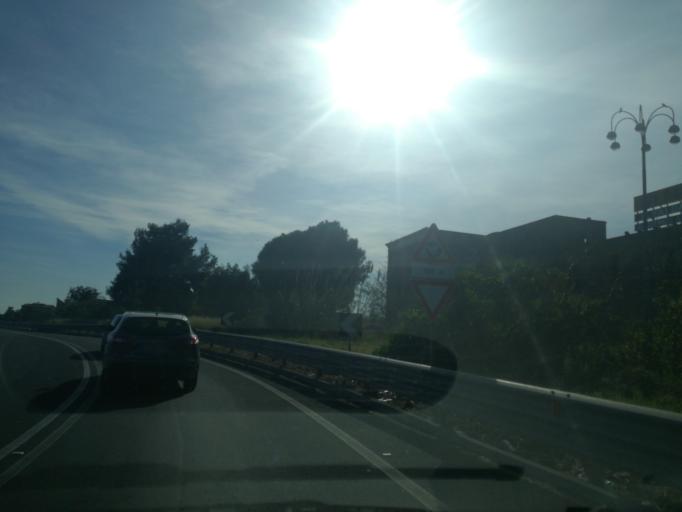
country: IT
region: Sicily
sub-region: Catania
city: Vambolieri
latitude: 37.5986
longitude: 15.1671
